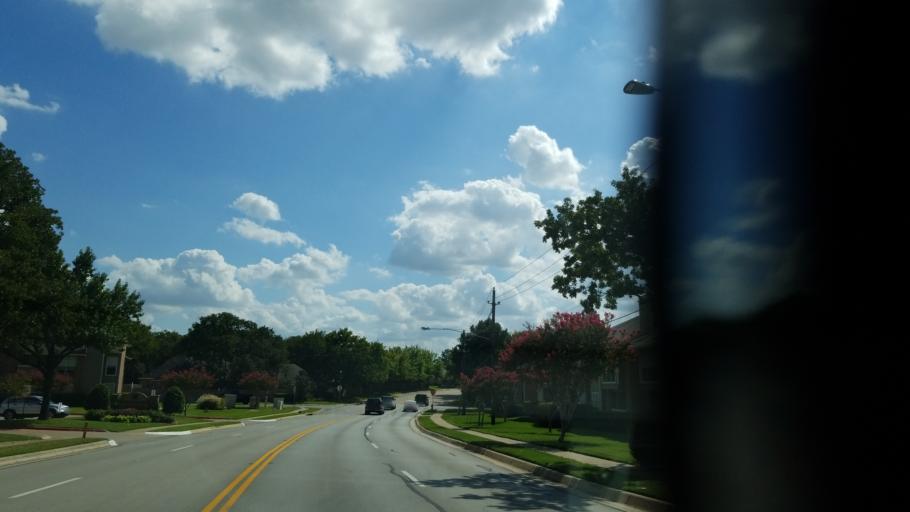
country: US
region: Texas
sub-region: Tarrant County
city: Bedford
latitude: 32.8490
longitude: -97.1171
